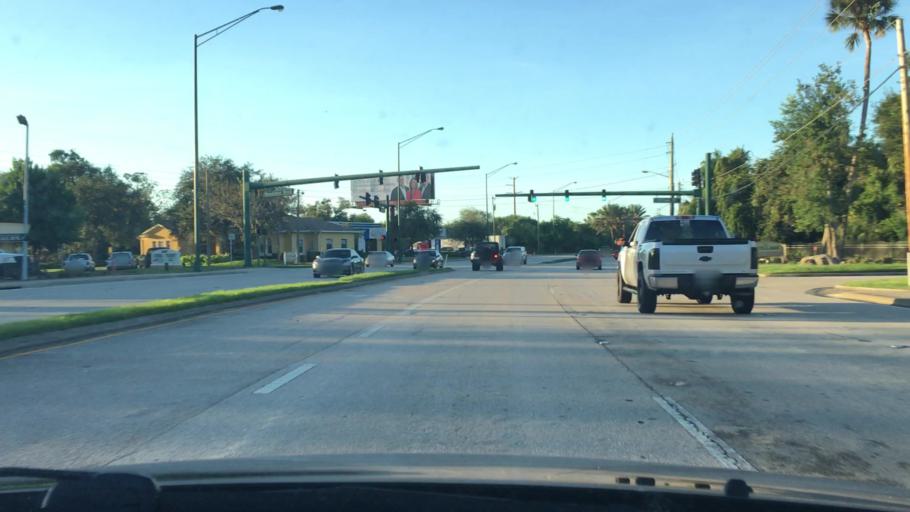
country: US
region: Florida
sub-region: Volusia County
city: Ormond Beach
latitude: 29.2733
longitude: -81.0824
